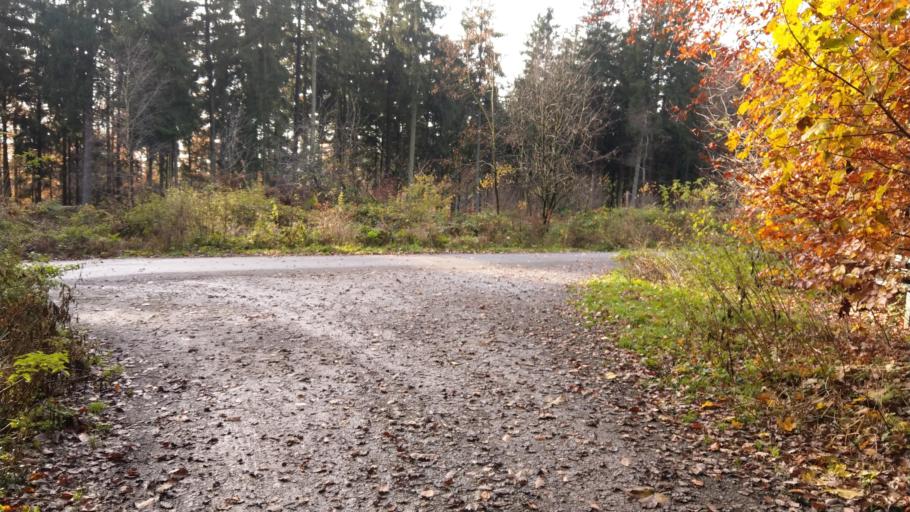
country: DE
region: North Rhine-Westphalia
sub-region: Regierungsbezirk Koln
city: Aachen
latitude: 50.7471
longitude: 6.0540
